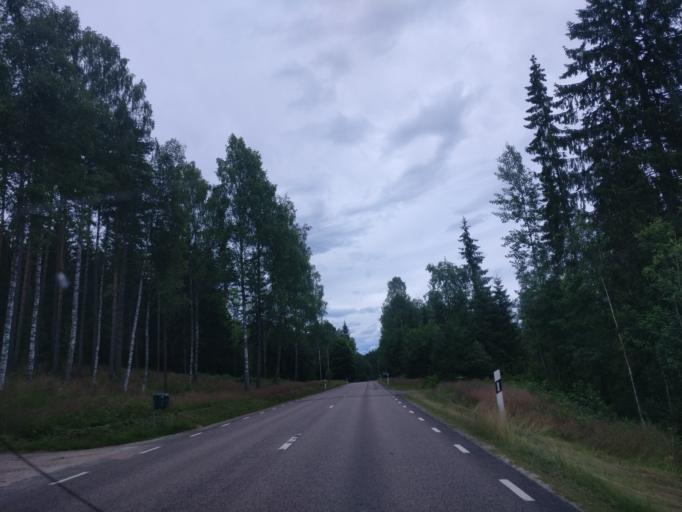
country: SE
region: Vaermland
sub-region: Hagfors Kommun
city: Ekshaerad
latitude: 60.1649
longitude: 13.4767
